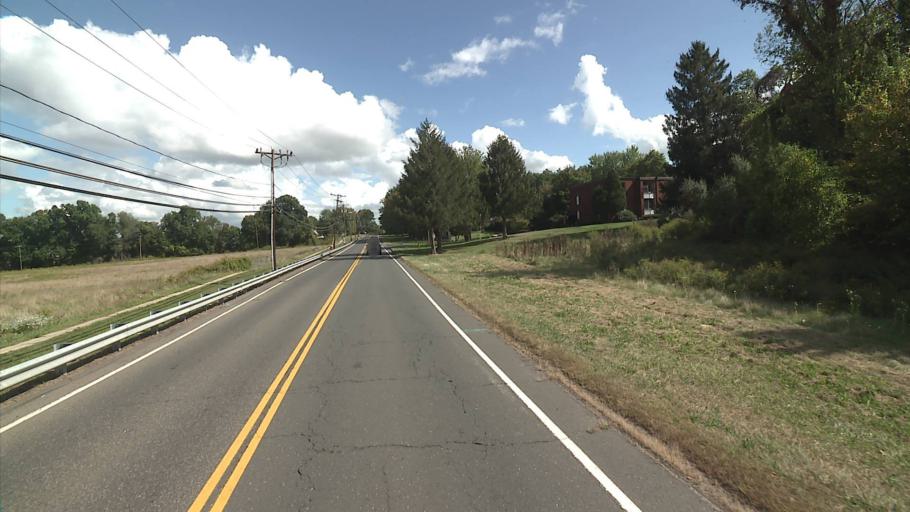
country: US
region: Connecticut
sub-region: Middlesex County
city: Cromwell
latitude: 41.6537
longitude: -72.6472
